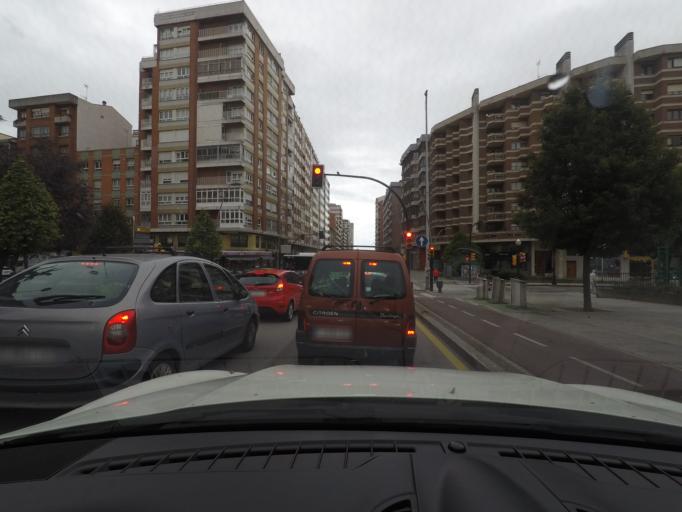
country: ES
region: Asturias
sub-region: Province of Asturias
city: Gijon
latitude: 43.5359
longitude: -5.6480
